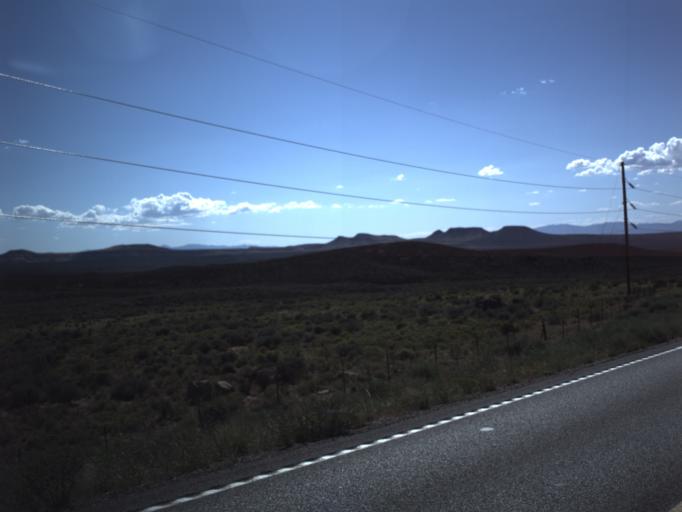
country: US
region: Utah
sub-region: Washington County
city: LaVerkin
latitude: 37.1232
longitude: -113.1951
